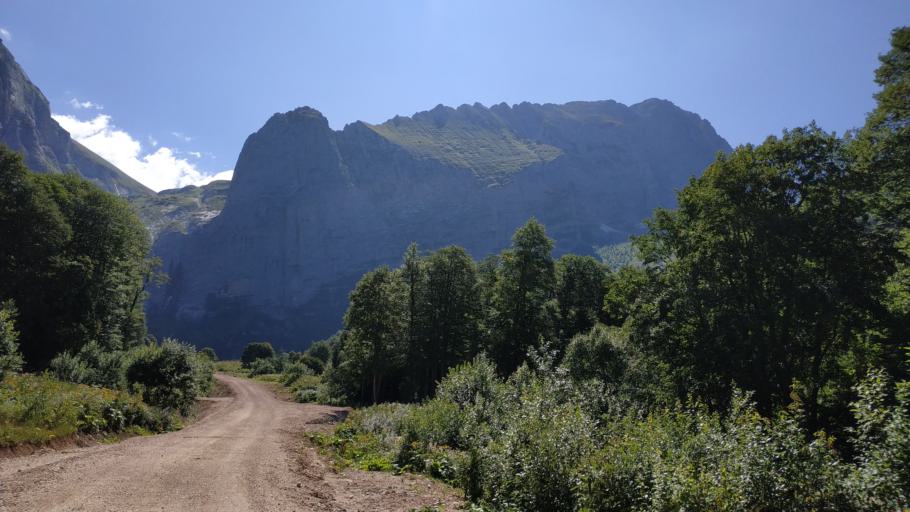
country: RU
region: Krasnodarskiy
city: Dagomys
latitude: 43.9797
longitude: 39.8664
